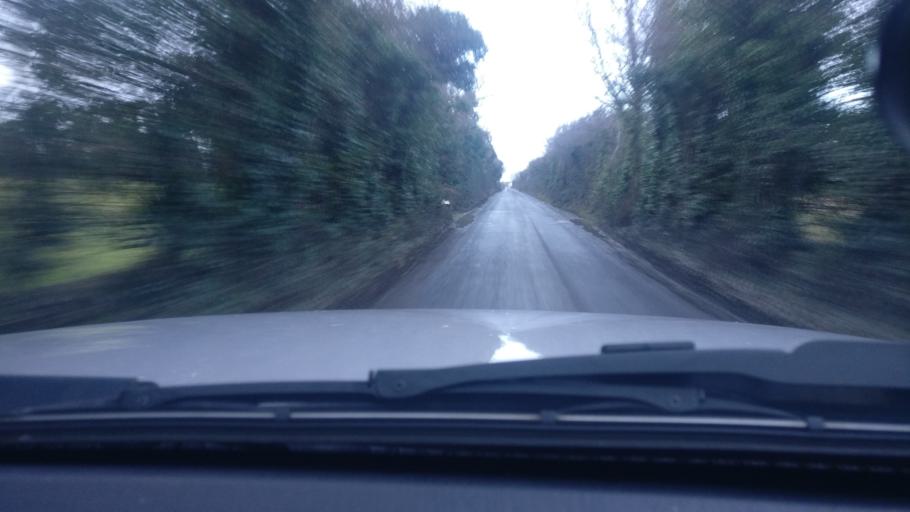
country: IE
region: Connaught
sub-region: County Galway
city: Loughrea
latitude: 53.1950
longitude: -8.5089
